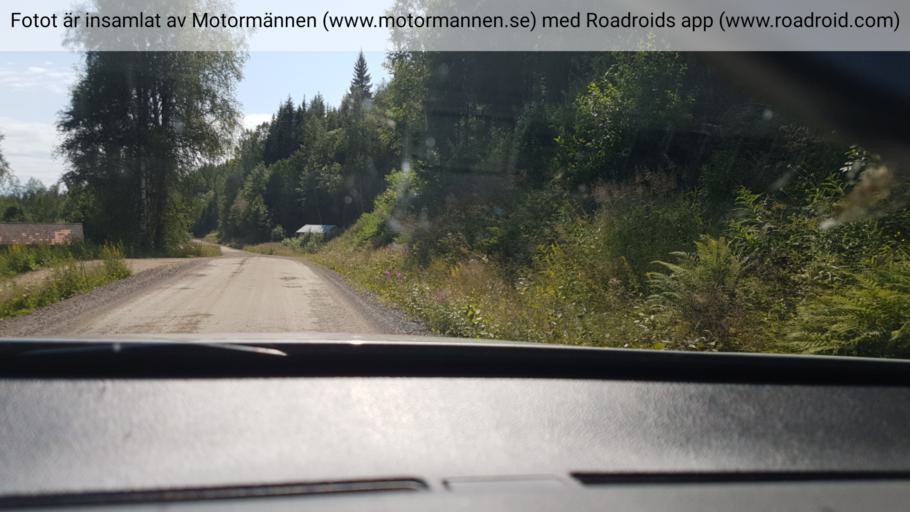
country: SE
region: Vaermland
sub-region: Torsby Kommun
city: Torsby
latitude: 60.4400
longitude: 13.2243
